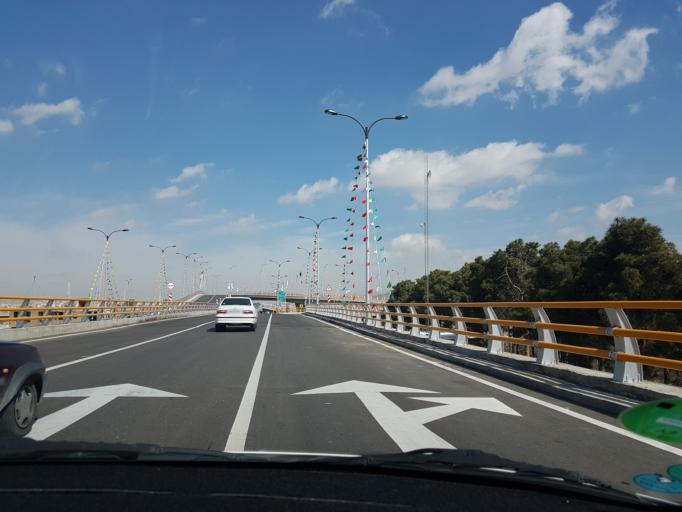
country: IR
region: Fars
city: Shiraz
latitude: 29.6140
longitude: 52.4683
